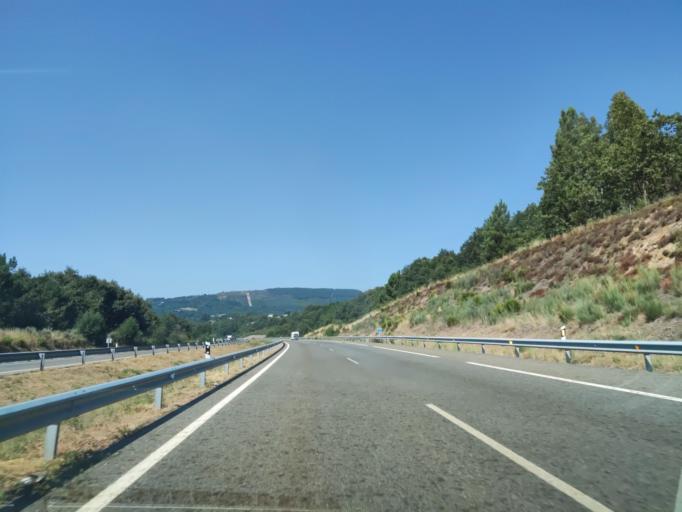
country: ES
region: Galicia
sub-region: Provincia de Ourense
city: Rios
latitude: 41.9805
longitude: -7.3049
